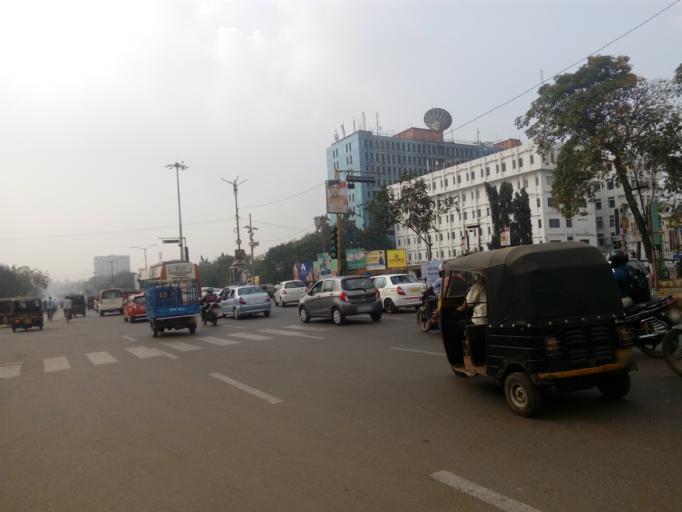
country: IN
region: Odisha
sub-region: Khordha
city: Bhubaneshwar
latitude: 20.2899
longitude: 85.8429
